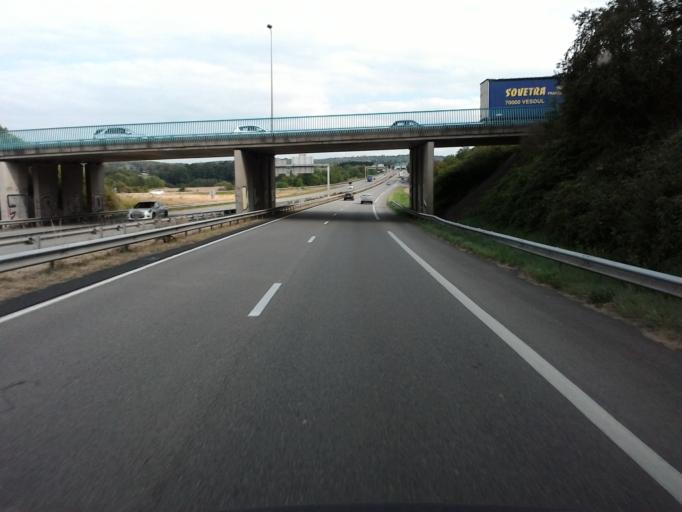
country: FR
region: Lorraine
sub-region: Departement des Vosges
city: Epinal
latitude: 48.1977
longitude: 6.4728
